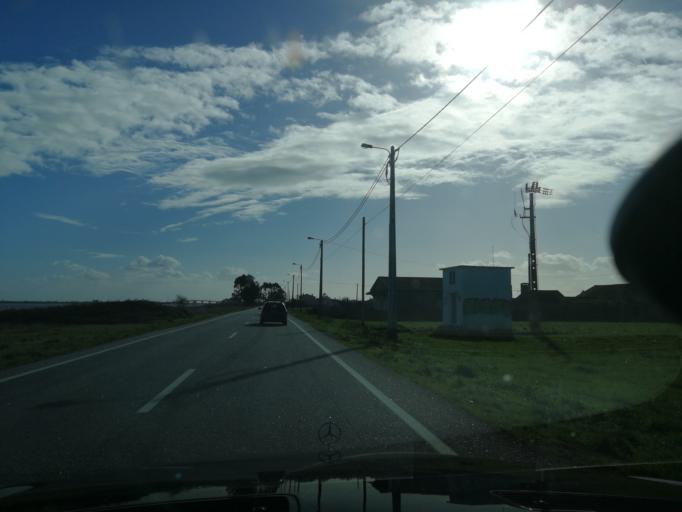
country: PT
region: Aveiro
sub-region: Estarreja
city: Pardilho
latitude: 40.8085
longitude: -8.6720
